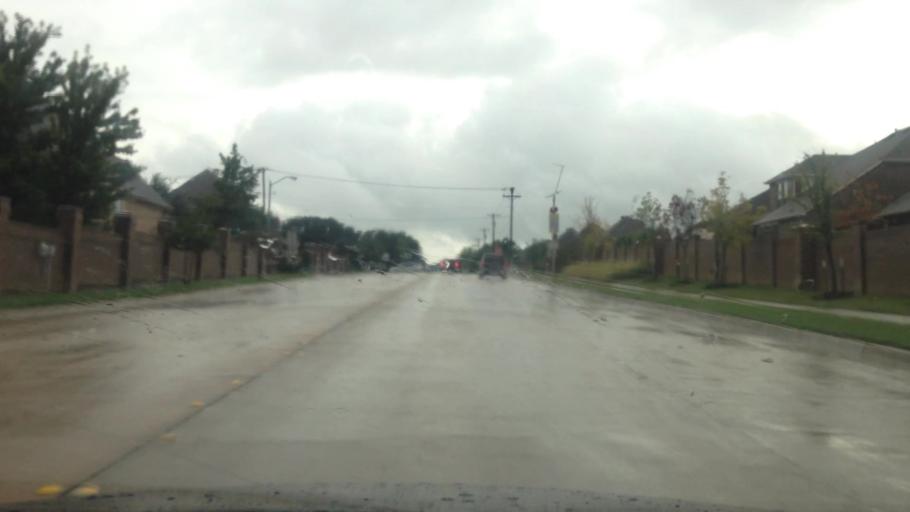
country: US
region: Texas
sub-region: Tarrant County
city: Watauga
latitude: 32.8930
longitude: -97.2104
